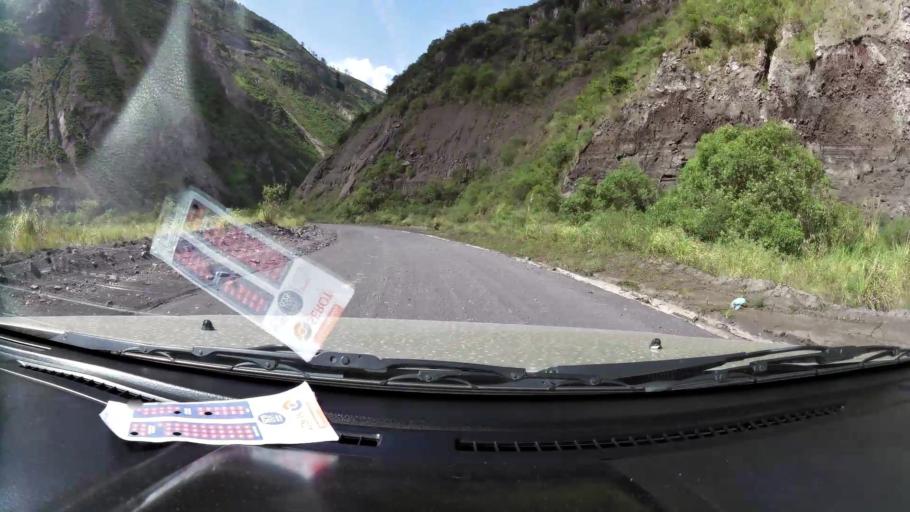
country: EC
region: Tungurahua
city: Banos
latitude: -1.4750
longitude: -78.5118
